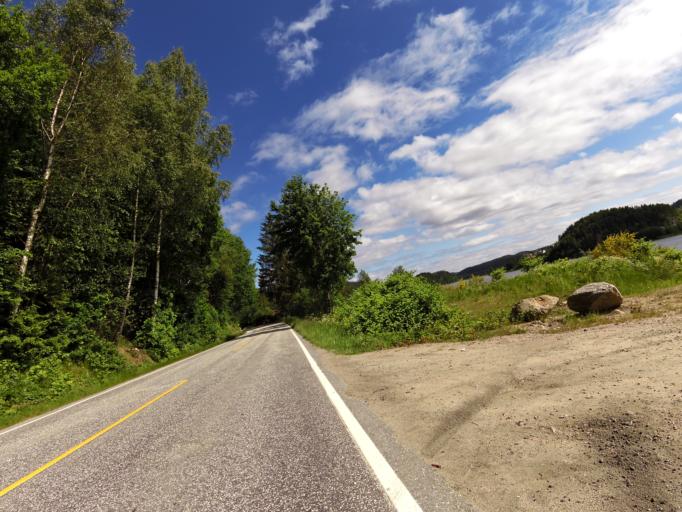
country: NO
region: Vest-Agder
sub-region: Vennesla
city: Vennesla
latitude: 58.2713
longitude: 7.9538
